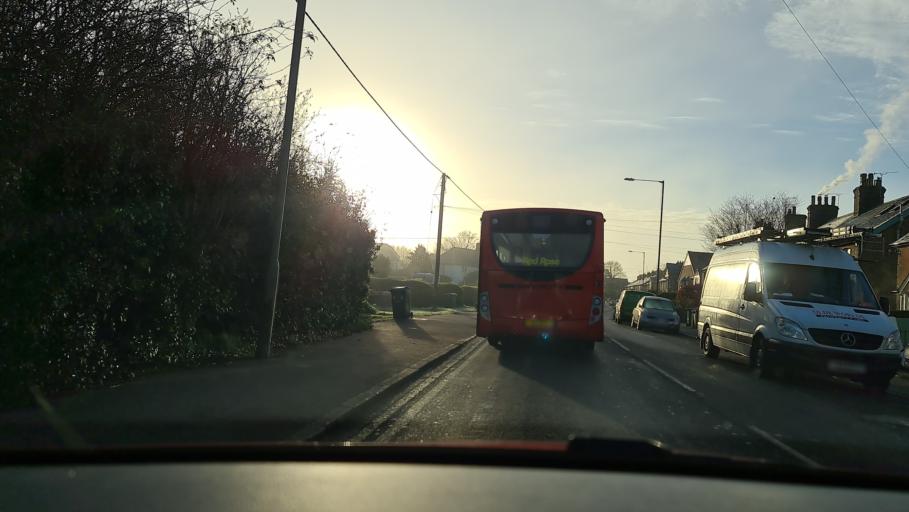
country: GB
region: England
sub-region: Buckinghamshire
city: Wendover
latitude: 51.7672
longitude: -0.7447
